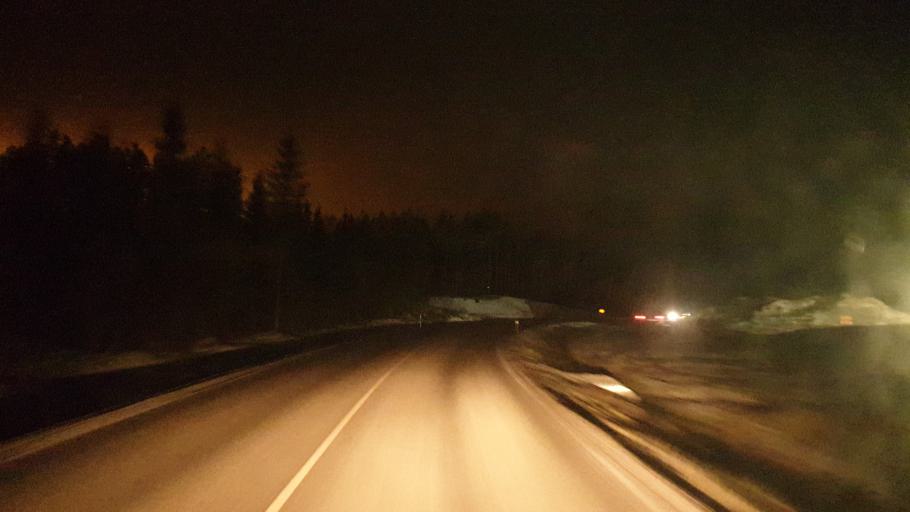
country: FI
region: Southern Savonia
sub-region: Pieksaemaeki
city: Juva
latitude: 61.8652
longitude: 27.7354
